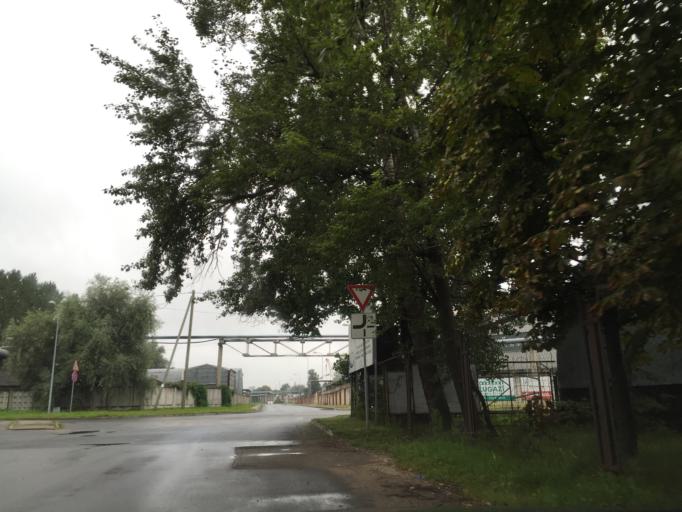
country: LV
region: Riga
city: Riga
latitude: 56.9821
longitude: 24.1107
